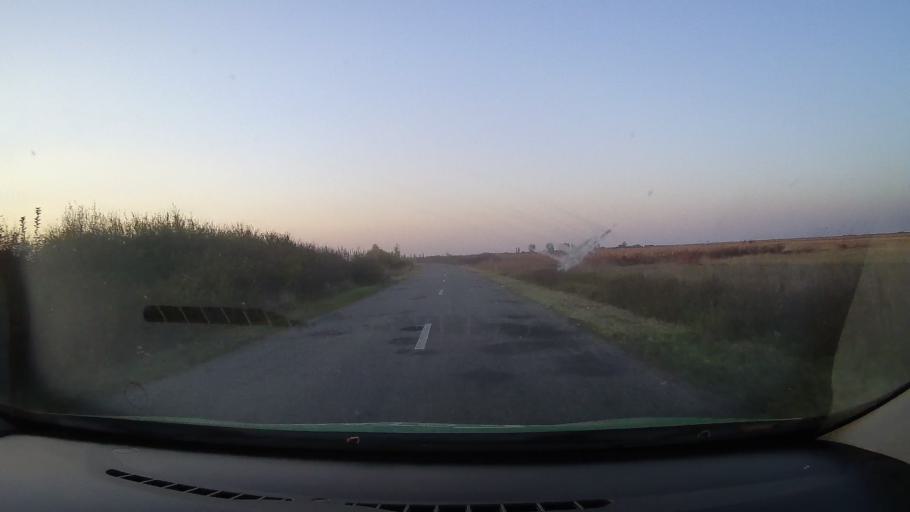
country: RO
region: Arad
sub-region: Comuna Zarand
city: Zarand
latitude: 46.3894
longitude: 21.6618
